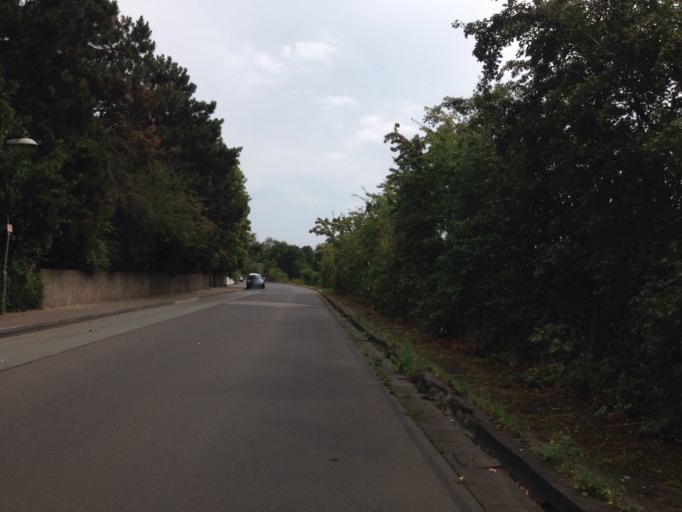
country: DE
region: Hesse
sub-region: Regierungsbezirk Giessen
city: Giessen
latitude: 50.5789
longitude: 8.6889
